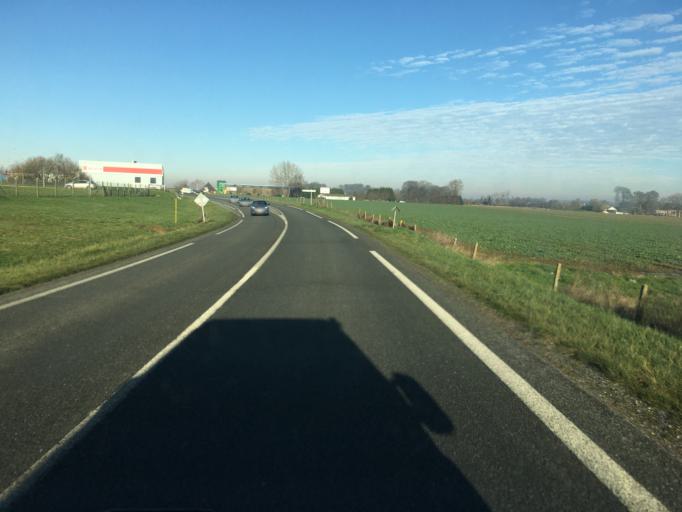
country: FR
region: Haute-Normandie
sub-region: Departement de la Seine-Maritime
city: Sainte-Marie-des-Champs
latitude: 49.6212
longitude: 0.7906
